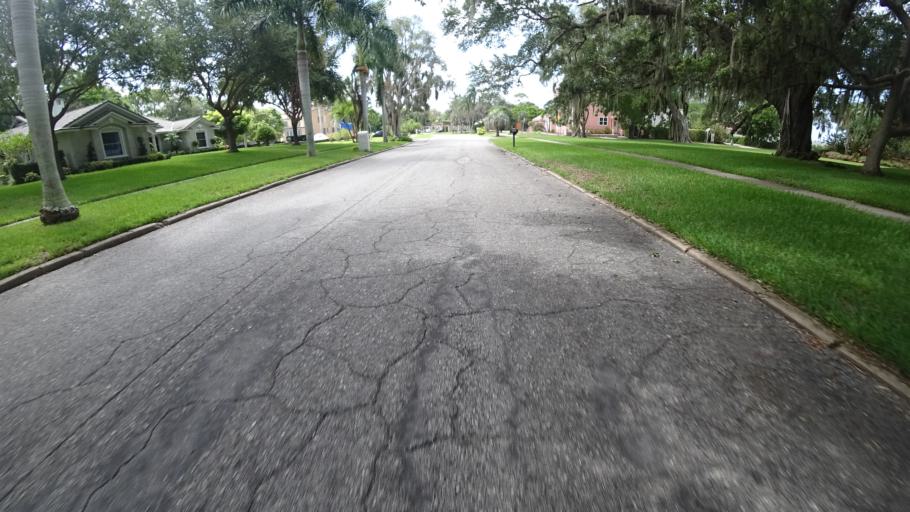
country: US
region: Florida
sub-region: Manatee County
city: Whitfield
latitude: 27.4044
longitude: -82.5714
